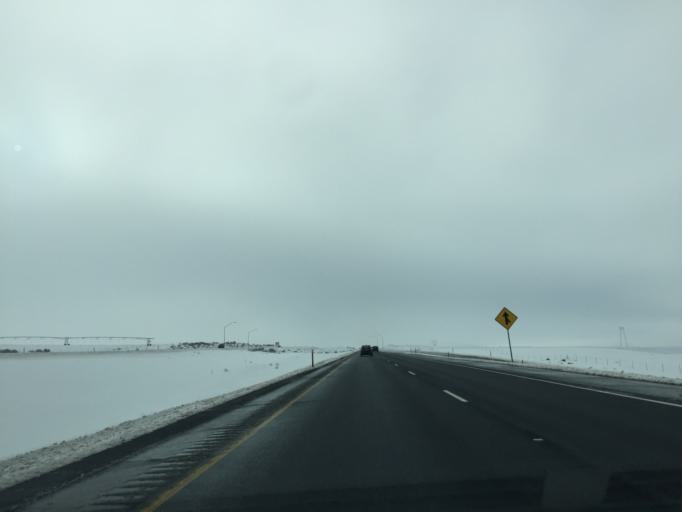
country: US
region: Washington
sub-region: Grant County
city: Quincy
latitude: 47.0199
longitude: -119.9458
